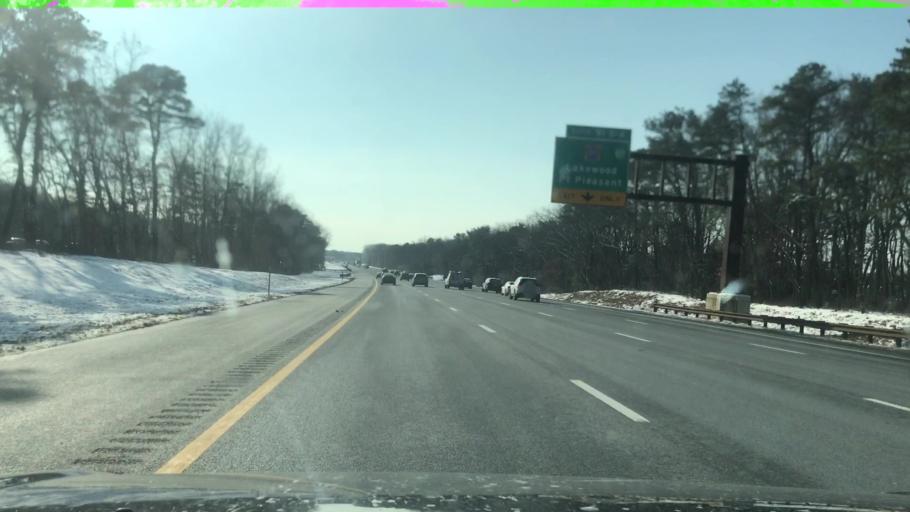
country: US
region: New Jersey
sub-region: Monmouth County
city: Ramtown
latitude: 40.1122
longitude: -74.1335
